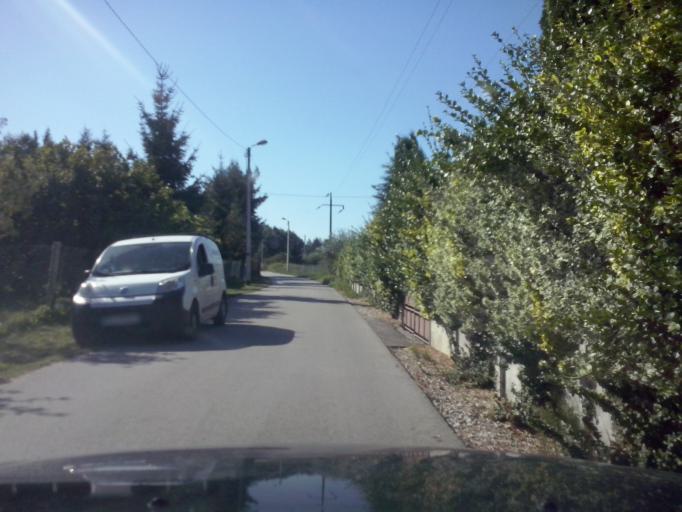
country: PL
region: Swietokrzyskie
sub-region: Powiat kielecki
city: Chmielnik
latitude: 50.6131
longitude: 20.7211
